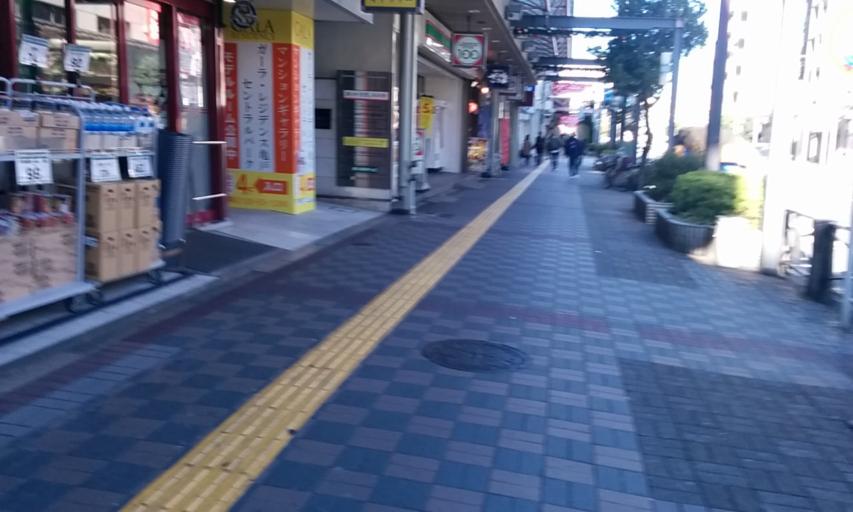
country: JP
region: Tokyo
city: Urayasu
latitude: 35.7001
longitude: 139.8255
